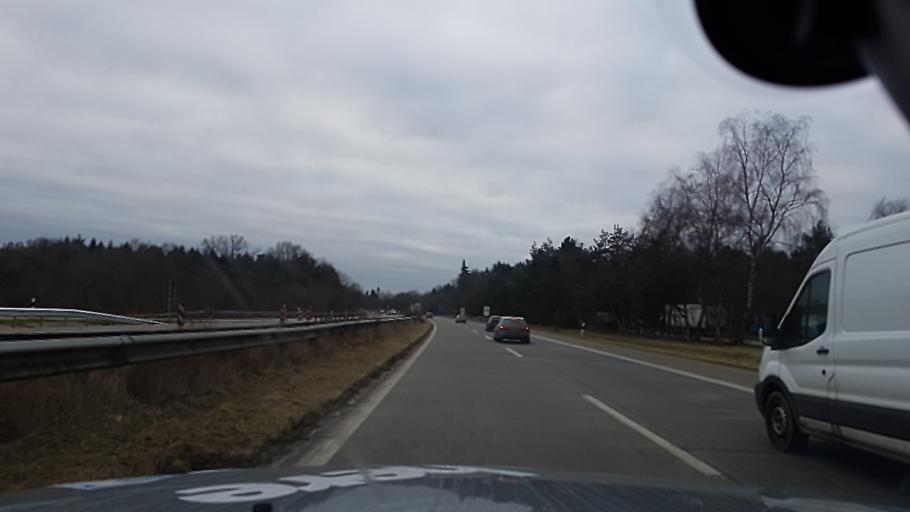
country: DE
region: Schleswig-Holstein
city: Ratekau
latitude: 53.9317
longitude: 10.7305
